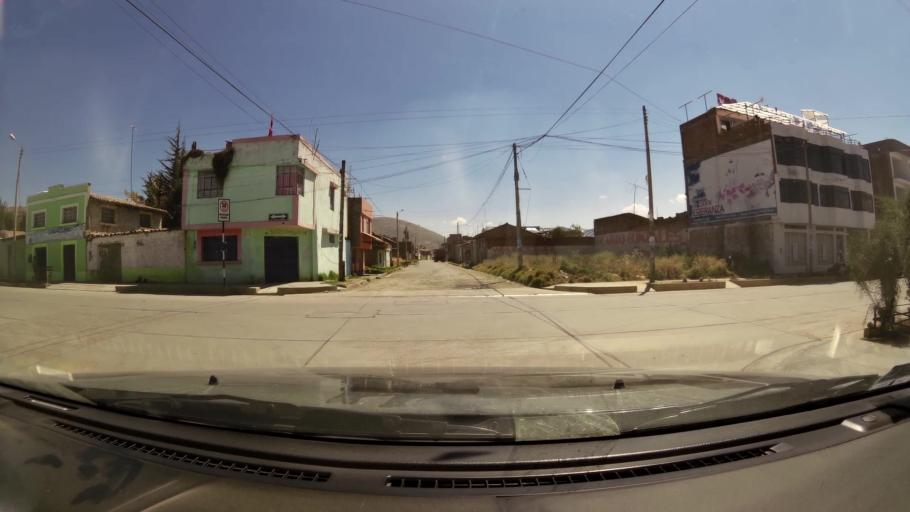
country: PE
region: Junin
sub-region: Provincia de Jauja
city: Jauja
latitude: -11.7691
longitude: -75.5004
